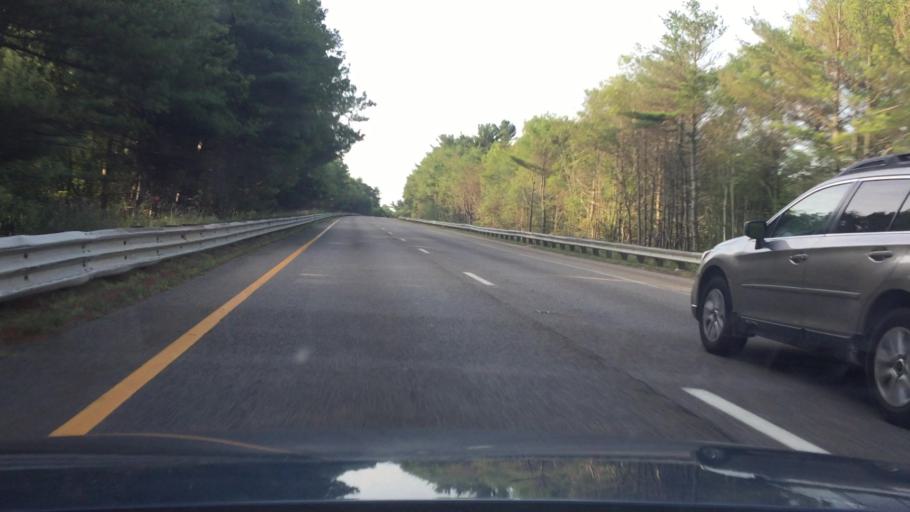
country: US
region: Massachusetts
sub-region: Plymouth County
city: Marshfield
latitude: 42.0695
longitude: -70.7311
